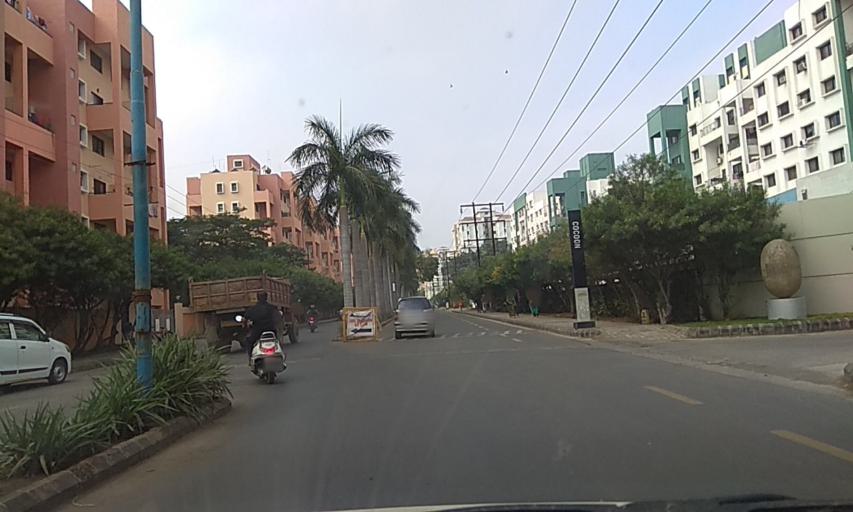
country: IN
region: Maharashtra
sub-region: Pune Division
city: Pune
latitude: 18.5088
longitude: 73.9279
